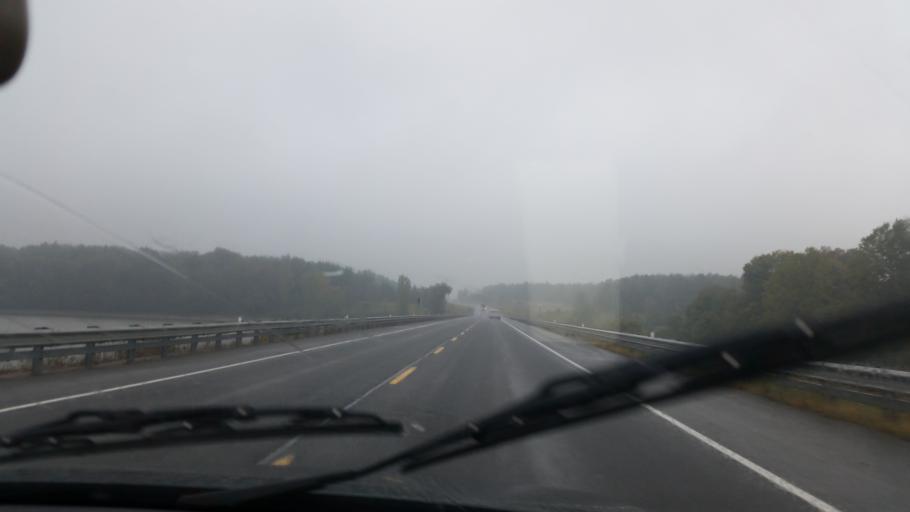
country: CA
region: Ontario
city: Stratford
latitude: 43.2626
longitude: -81.0743
